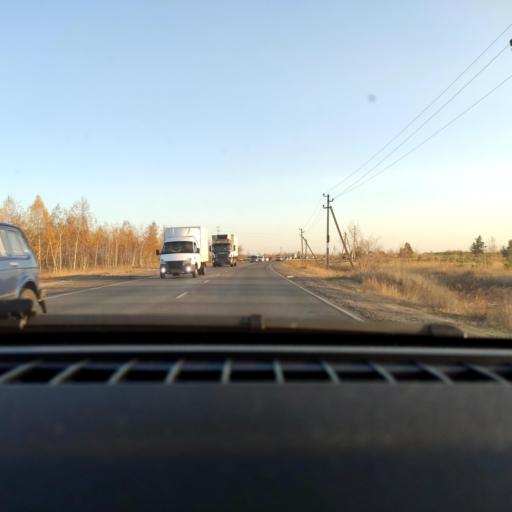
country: RU
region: Voronezj
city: Maslovka
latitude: 51.5791
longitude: 39.2644
